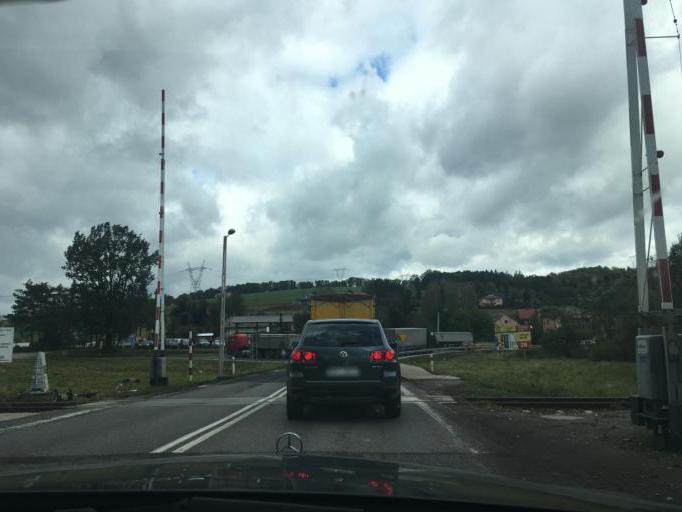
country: PL
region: Subcarpathian Voivodeship
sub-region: Powiat strzyzowski
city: Babica
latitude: 49.9337
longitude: 21.8709
